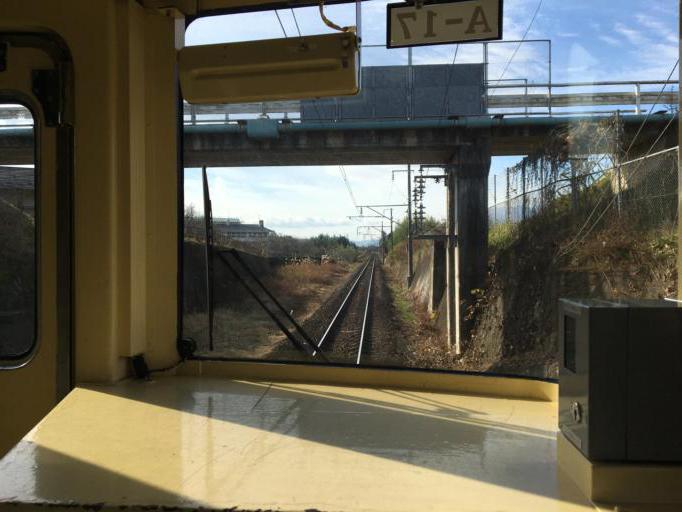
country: JP
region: Fukushima
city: Yanagawamachi-saiwaicho
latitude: 37.8734
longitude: 140.6264
